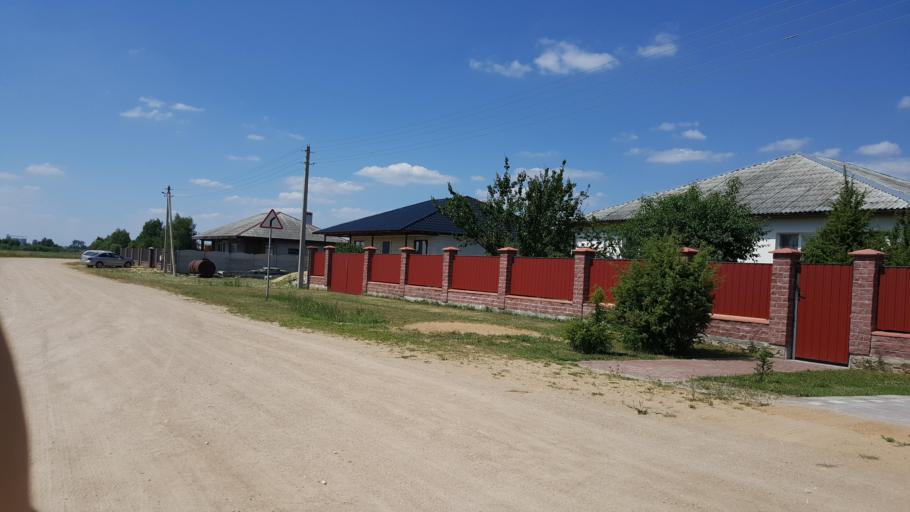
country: BY
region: Brest
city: Kamyanyets
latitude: 52.3913
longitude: 23.8140
